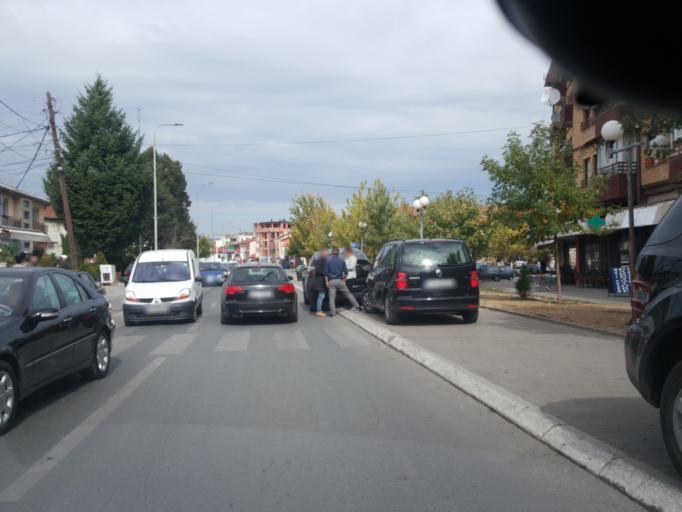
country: XK
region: Gjakova
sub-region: Komuna e Gjakoves
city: Gjakove
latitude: 42.3879
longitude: 20.4275
